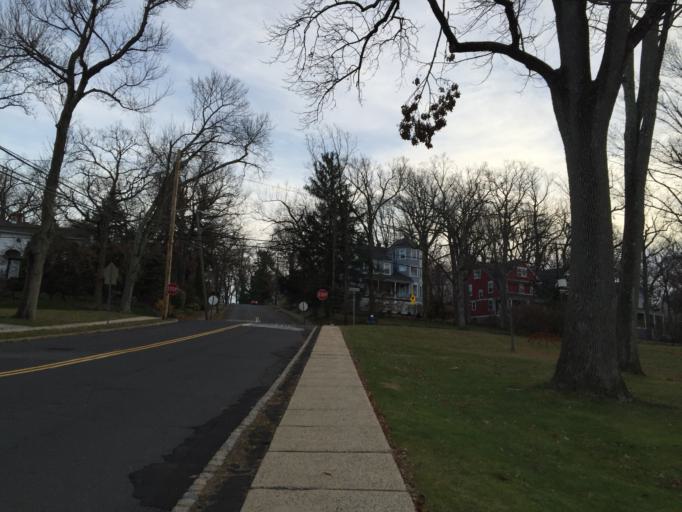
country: US
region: New Jersey
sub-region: Union County
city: Summit
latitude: 40.7104
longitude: -74.3588
